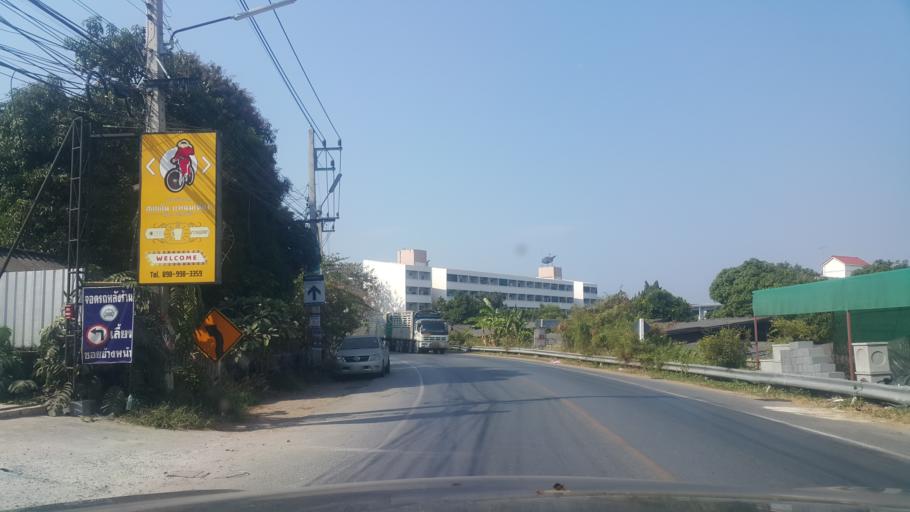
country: TH
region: Nakhon Ratchasima
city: Nakhon Ratchasima
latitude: 14.9489
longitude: 102.0441
